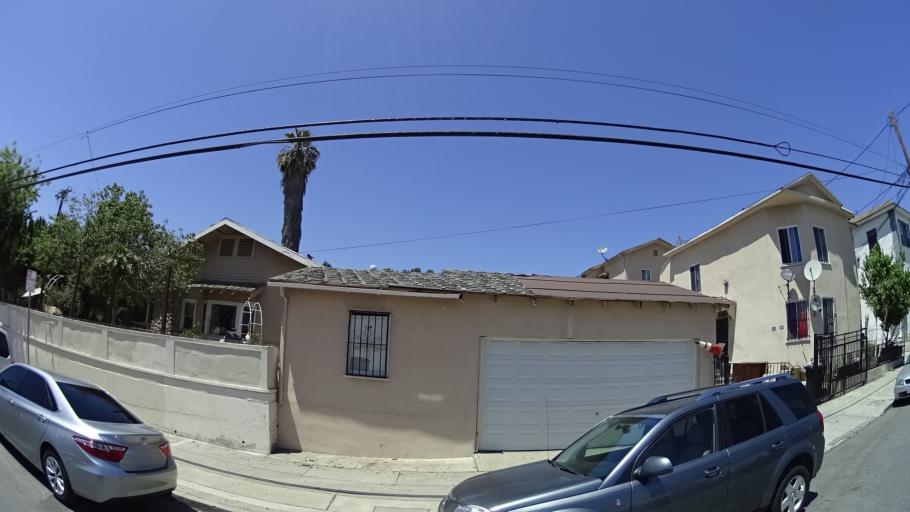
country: US
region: California
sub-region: Los Angeles County
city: Los Angeles
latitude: 34.0655
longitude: -118.2466
